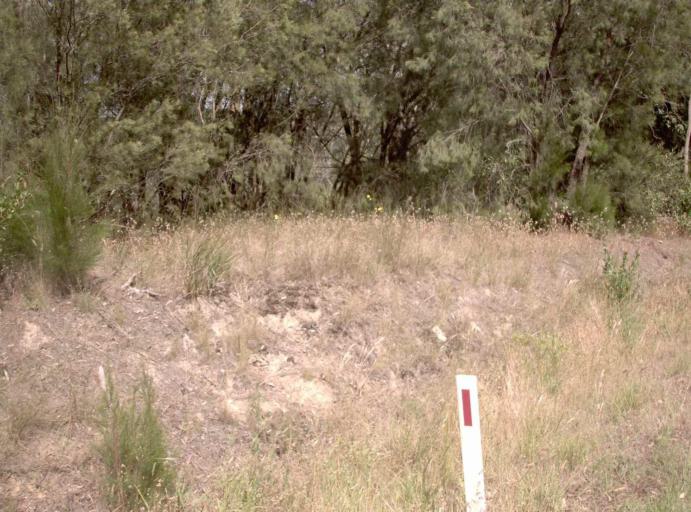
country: AU
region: Victoria
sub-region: Latrobe
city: Moe
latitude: -38.0832
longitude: 146.1952
